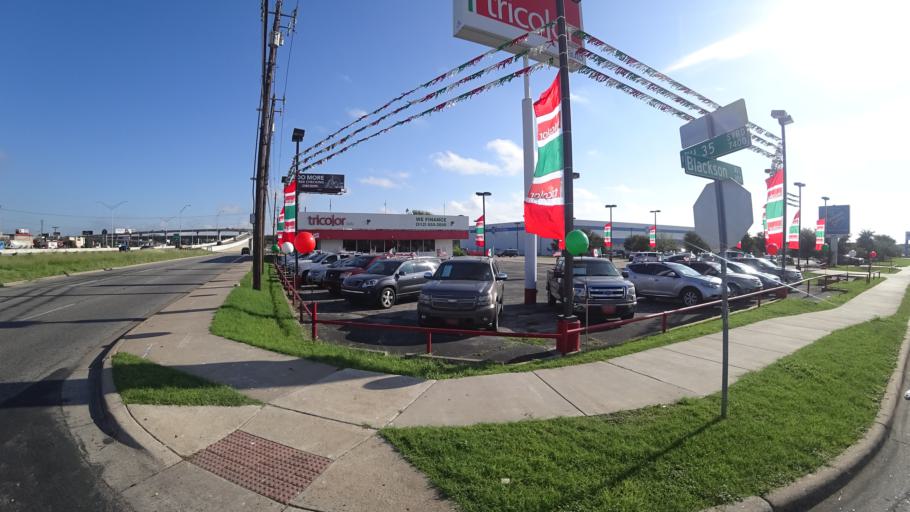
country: US
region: Texas
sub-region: Travis County
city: Austin
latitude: 30.3350
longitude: -97.7022
